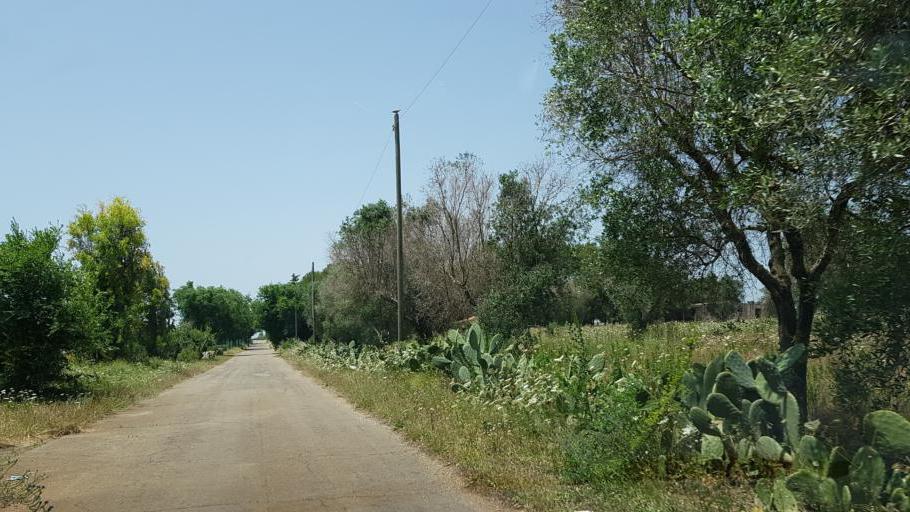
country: IT
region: Apulia
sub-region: Provincia di Lecce
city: Porto Cesareo
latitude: 40.3259
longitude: 17.8590
